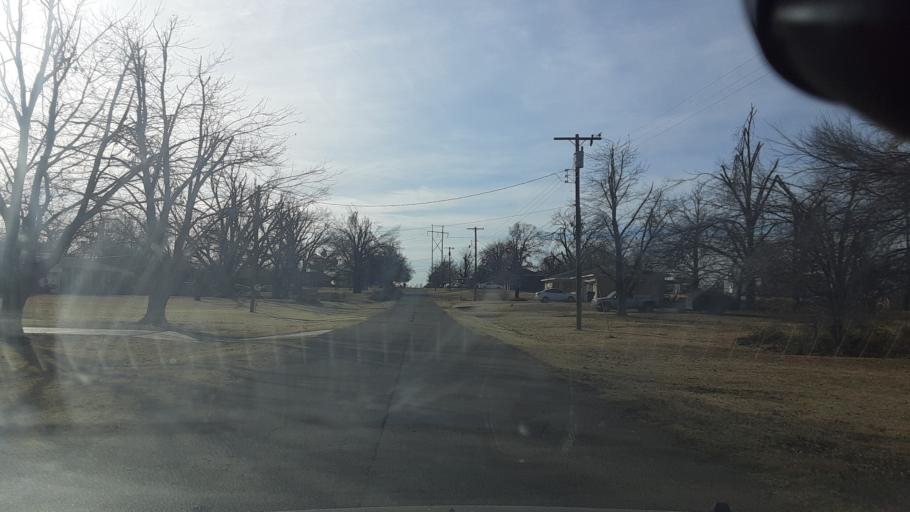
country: US
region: Oklahoma
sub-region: Logan County
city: Guthrie
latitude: 35.8559
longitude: -97.4331
